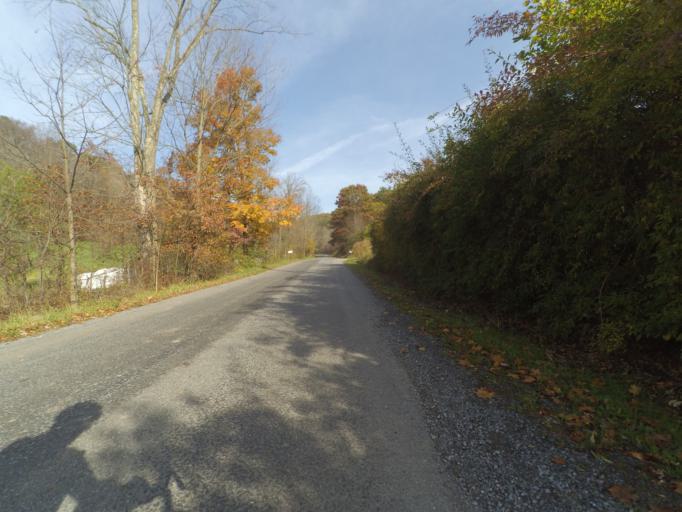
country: US
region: Pennsylvania
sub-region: Centre County
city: Park Forest Village
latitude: 40.9119
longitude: -77.9204
